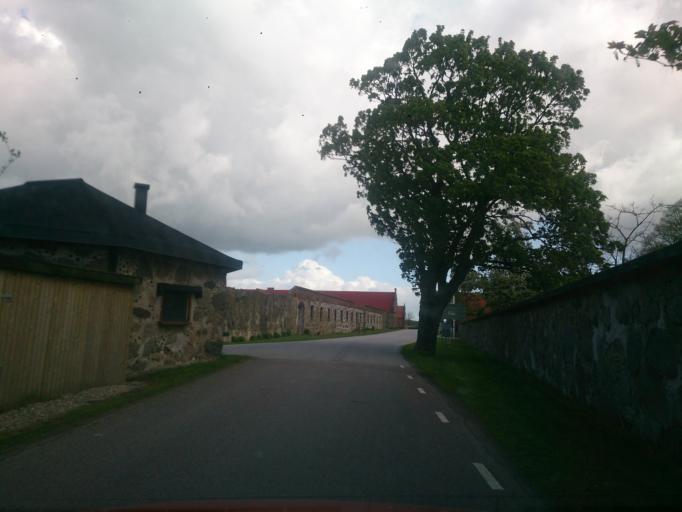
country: SE
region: Skane
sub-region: Ystads Kommun
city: Ystad
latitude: 55.4618
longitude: 13.7058
